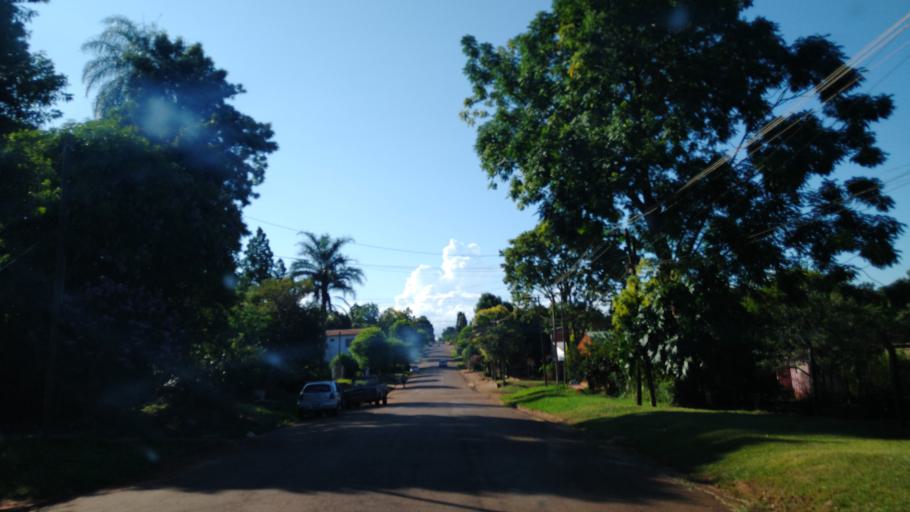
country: AR
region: Misiones
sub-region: Departamento de San Ignacio
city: San Ignacio
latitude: -27.2644
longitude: -55.5386
